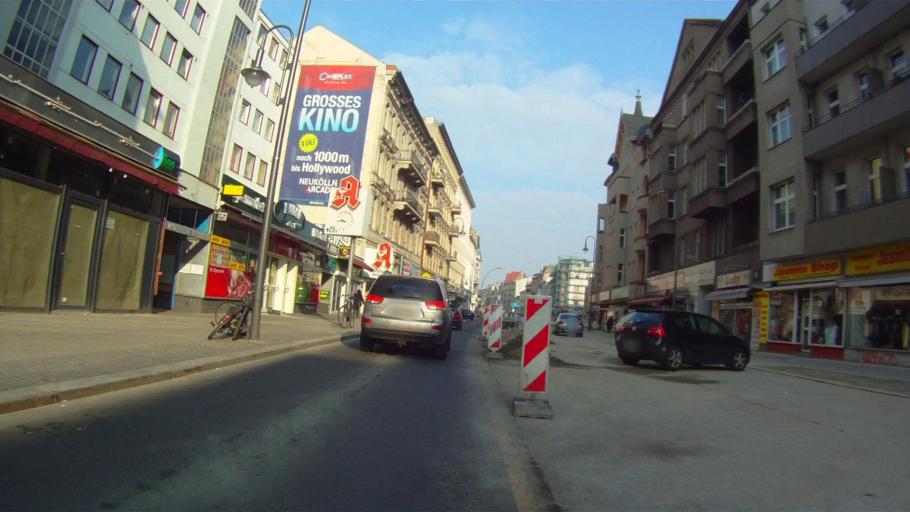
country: DE
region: Berlin
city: Berlin Treptow
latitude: 52.4746
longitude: 13.4401
